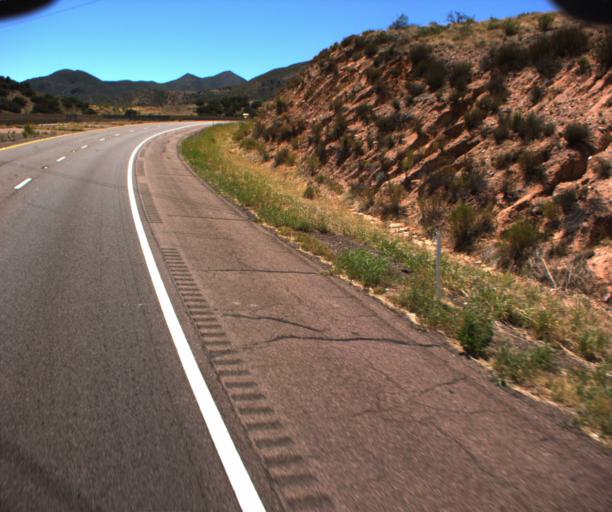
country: US
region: Arizona
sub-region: Gila County
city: Tonto Basin
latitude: 33.9920
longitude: -111.3713
